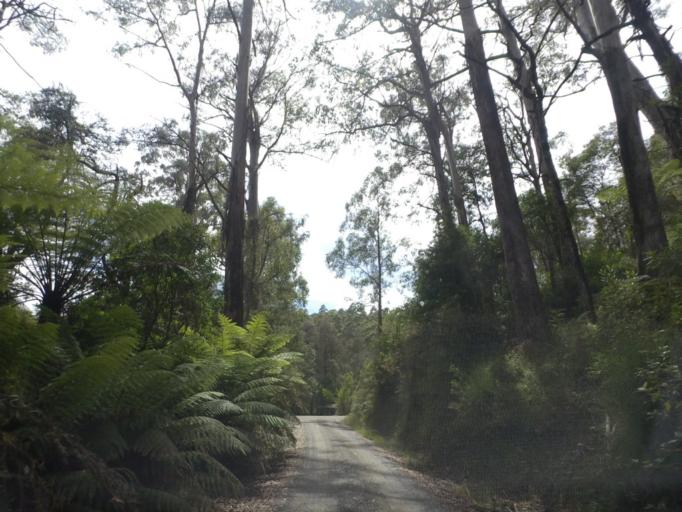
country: AU
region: Victoria
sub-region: Yarra Ranges
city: Healesville
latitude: -37.5279
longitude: 145.5205
